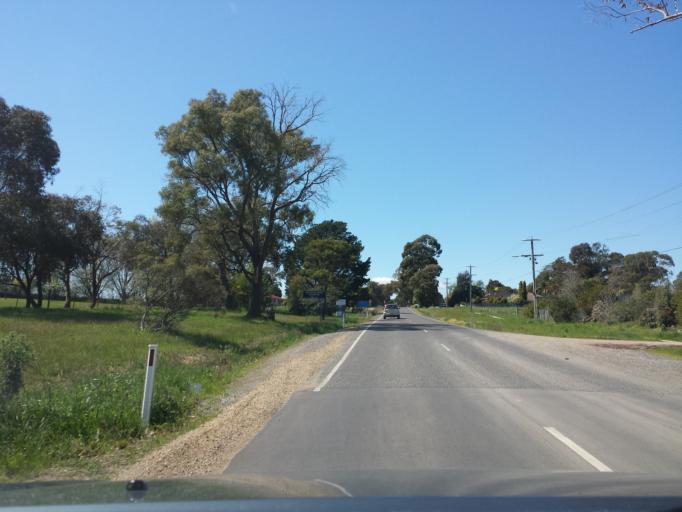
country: AU
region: Victoria
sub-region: Yarra Ranges
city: Lilydale
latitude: -37.7246
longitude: 145.3804
